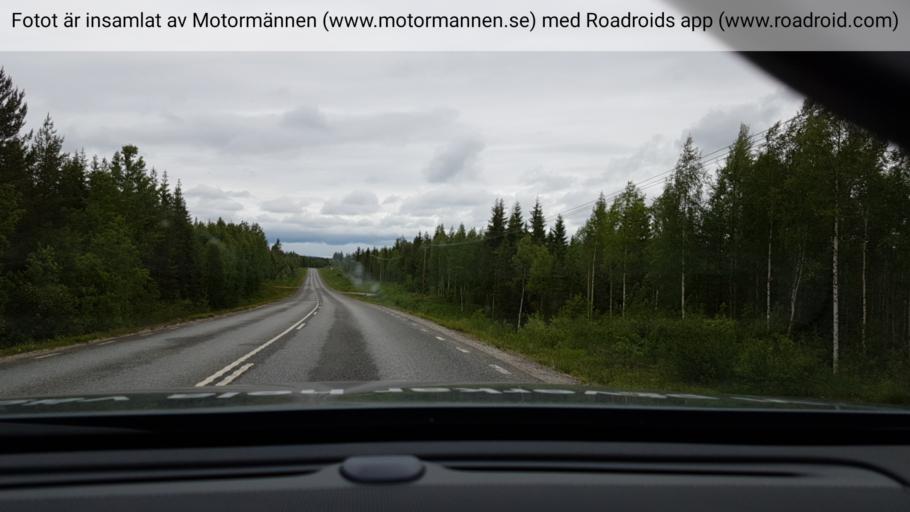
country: SE
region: Vaesterbotten
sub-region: Lycksele Kommun
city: Lycksele
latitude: 64.5433
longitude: 18.5037
